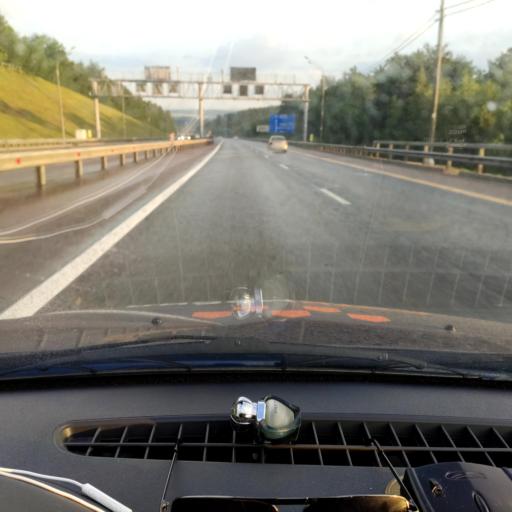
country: RU
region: Lipetsk
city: Zadonsk
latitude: 52.3647
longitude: 38.9295
